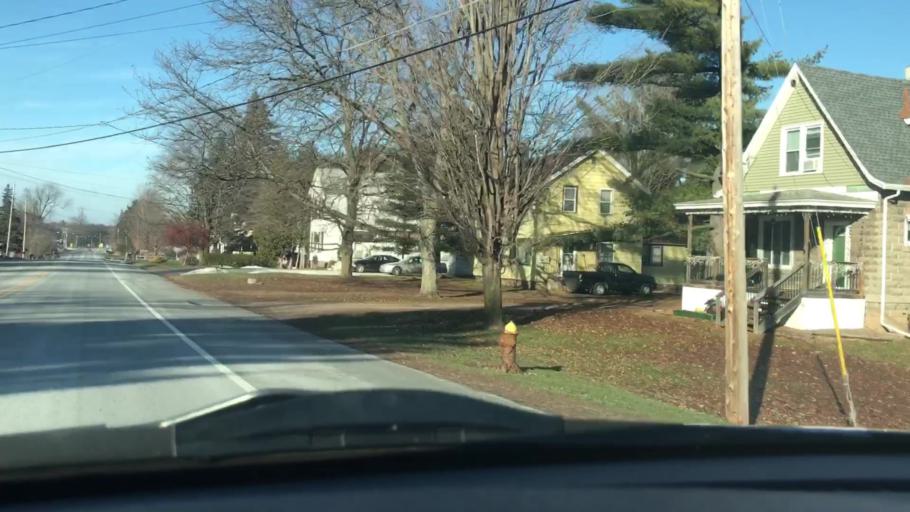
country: US
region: New York
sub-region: Madison County
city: Oneida
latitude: 43.0917
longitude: -75.6364
